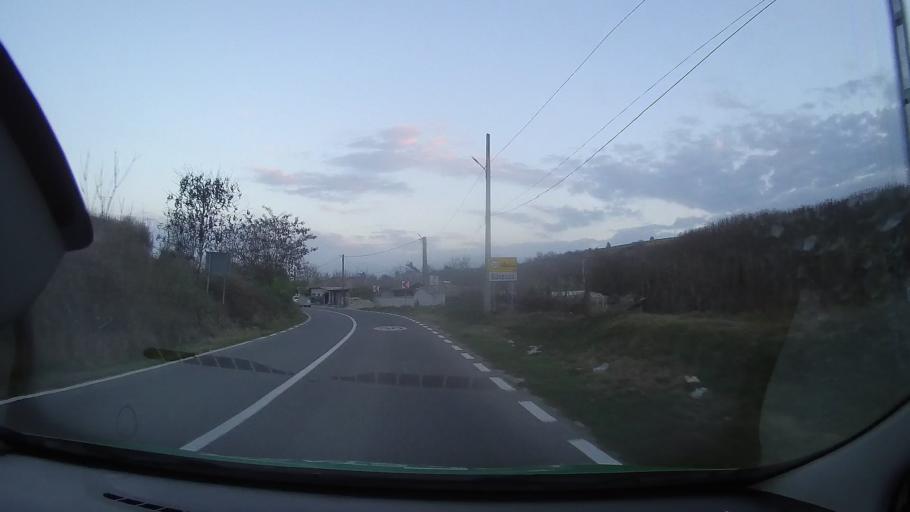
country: RO
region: Constanta
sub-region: Comuna Baneasa
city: Baneasa
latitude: 44.0753
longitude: 27.6794
